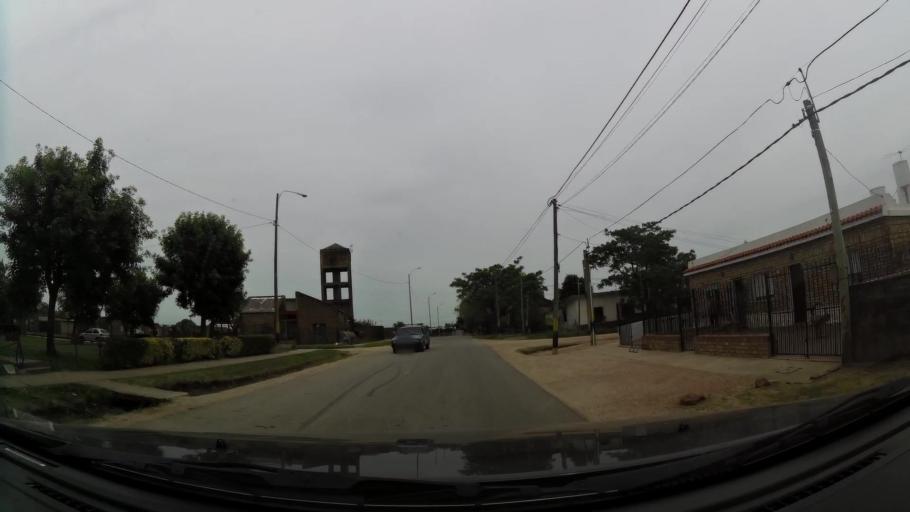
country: UY
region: Canelones
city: Las Piedras
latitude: -34.7421
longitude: -56.2259
